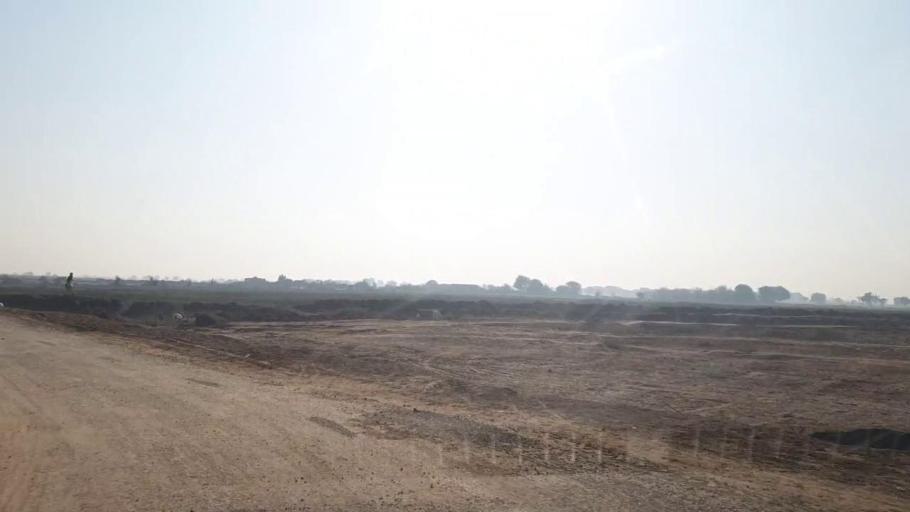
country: PK
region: Sindh
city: Shahpur Chakar
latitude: 26.0659
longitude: 68.5906
